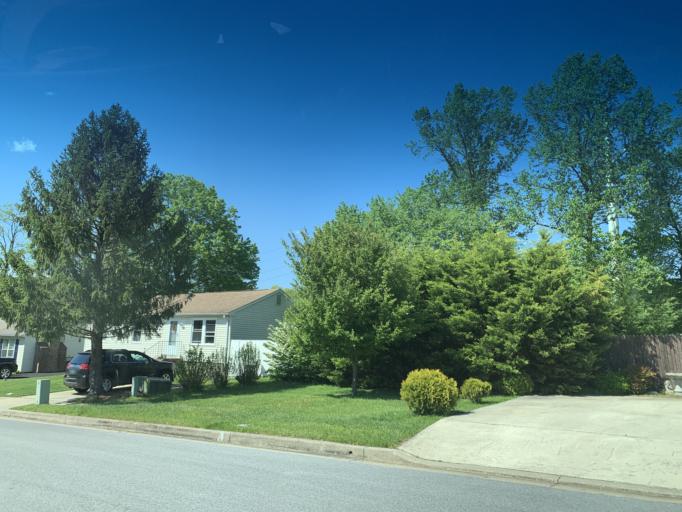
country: US
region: Maryland
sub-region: Baltimore County
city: White Marsh
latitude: 39.3636
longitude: -76.4317
